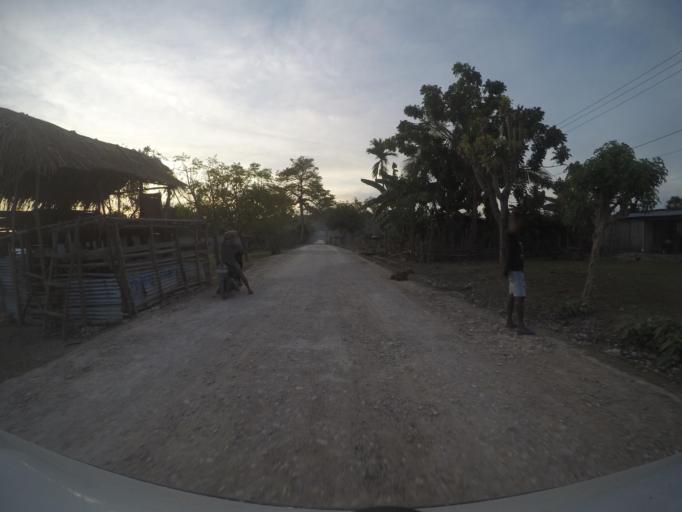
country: TL
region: Viqueque
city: Viqueque
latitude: -8.9265
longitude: 126.4059
